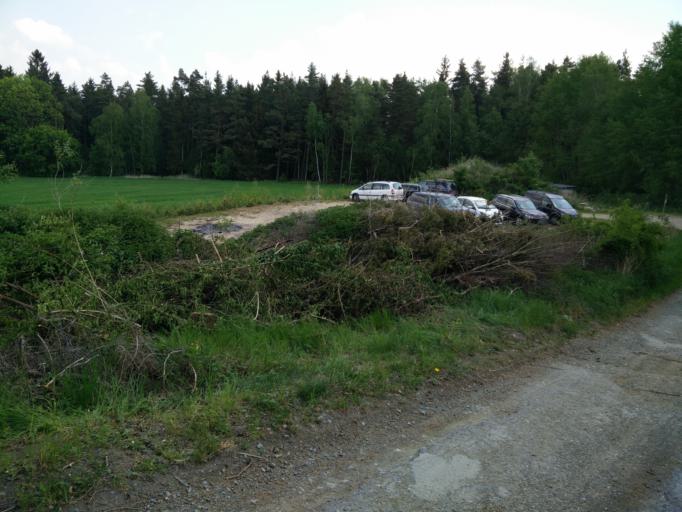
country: DE
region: Saxony
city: Triebel
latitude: 50.3784
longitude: 12.1330
